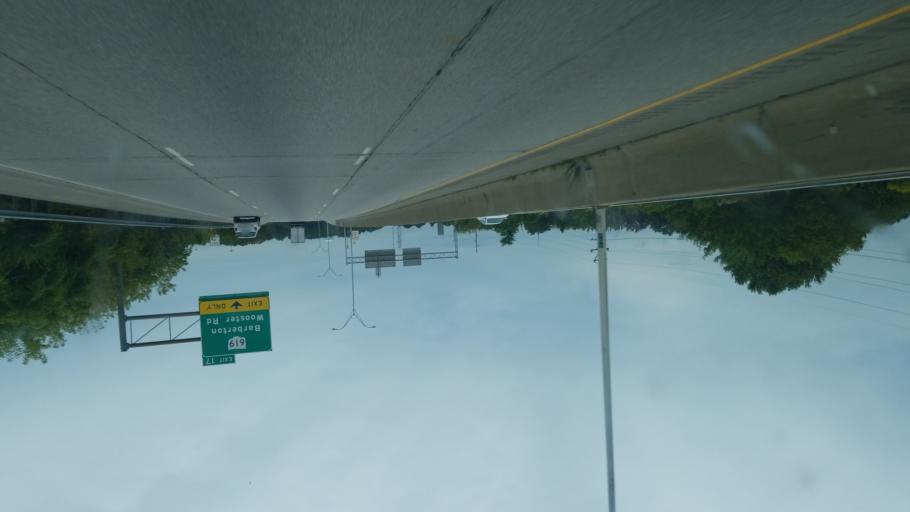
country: US
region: Ohio
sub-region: Summit County
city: Barberton
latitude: 41.0356
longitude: -81.5731
